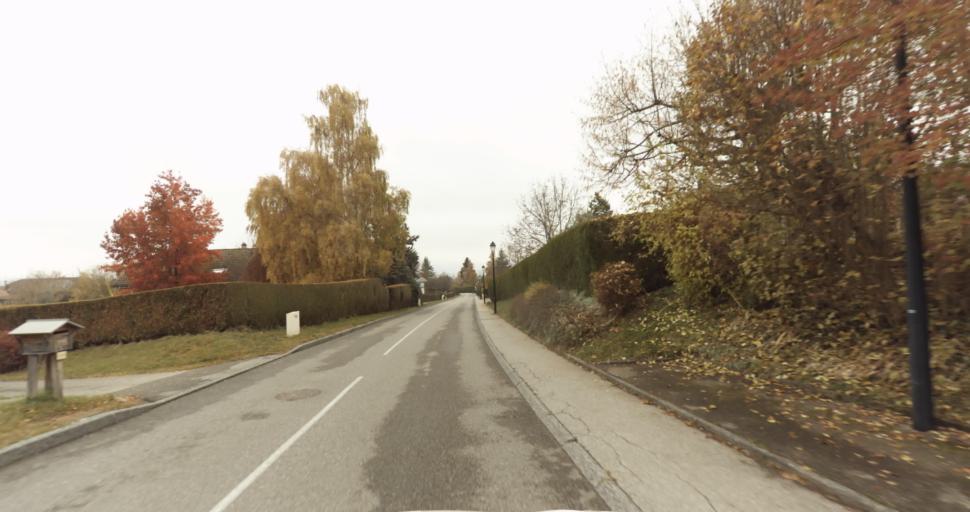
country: FR
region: Rhone-Alpes
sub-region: Departement de la Haute-Savoie
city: Seynod
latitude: 45.8464
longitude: 6.0845
